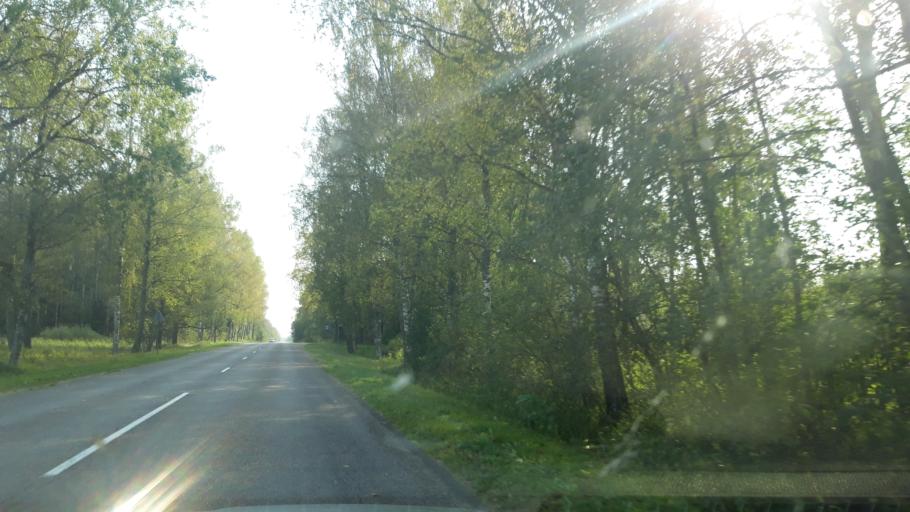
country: LV
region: Burtnieki
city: Matisi
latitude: 57.6540
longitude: 25.2324
